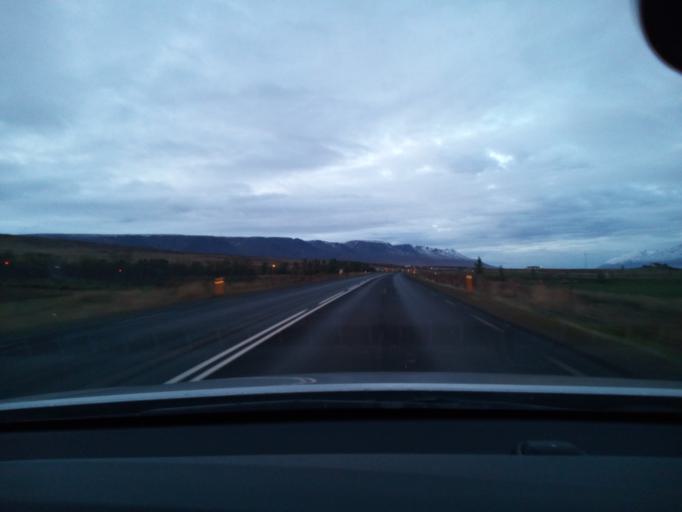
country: IS
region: Northeast
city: Akureyri
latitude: 65.7216
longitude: -18.1782
